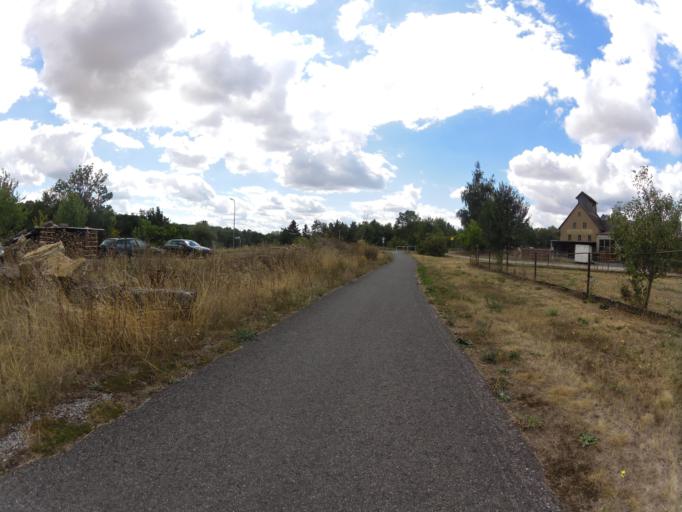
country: DE
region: Bavaria
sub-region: Regierungsbezirk Unterfranken
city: Aub
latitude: 49.5503
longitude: 10.0517
